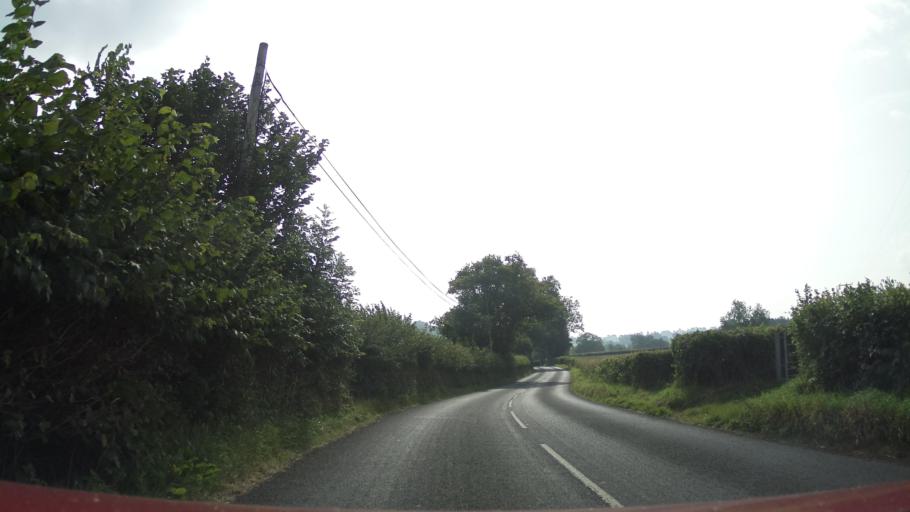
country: GB
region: England
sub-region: Bath and North East Somerset
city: East Harptree
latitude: 51.3006
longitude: -2.6075
